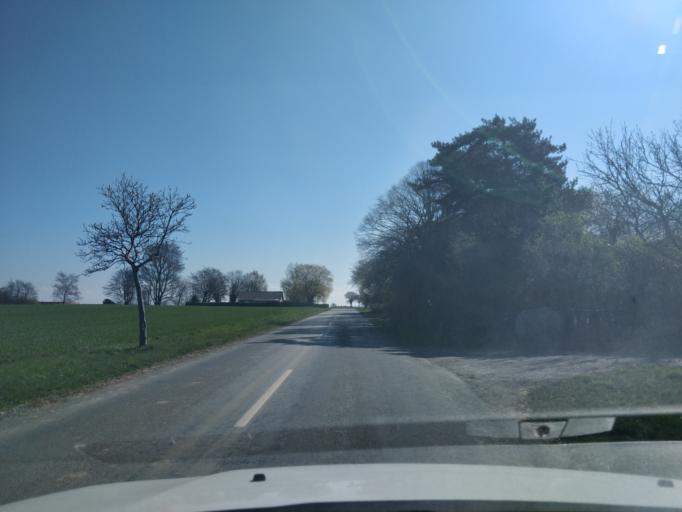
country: DK
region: Zealand
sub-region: Vordingborg Kommune
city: Stege
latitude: 54.9857
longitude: 12.3910
